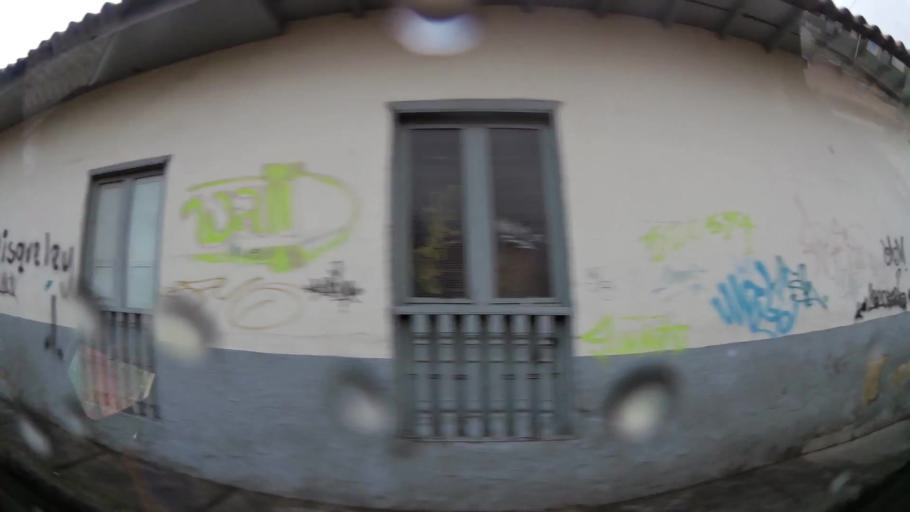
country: CO
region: Cundinamarca
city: Chia
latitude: 4.8604
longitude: -74.0591
